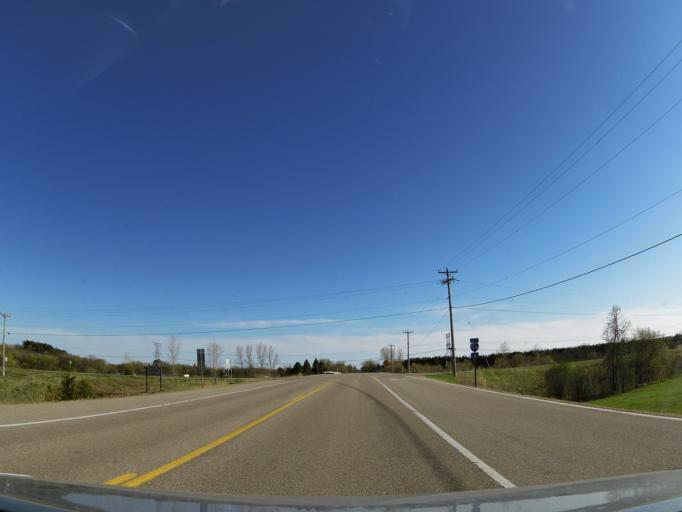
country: US
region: Minnesota
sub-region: Washington County
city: Lake Elmo
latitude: 44.9507
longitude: -92.8428
